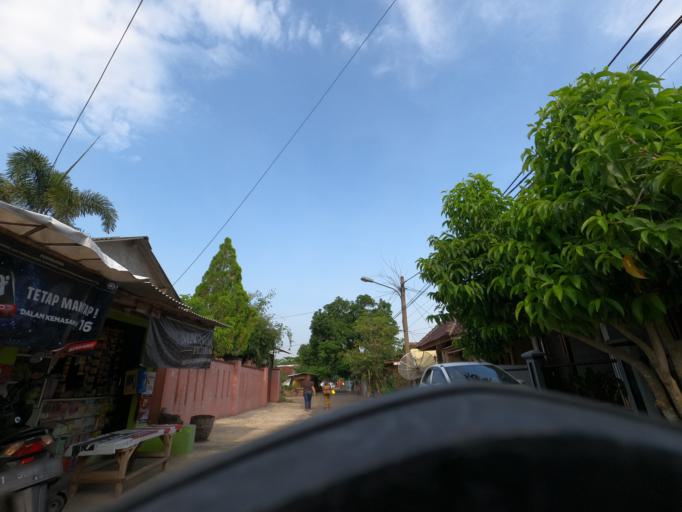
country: ID
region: West Java
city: Lembang
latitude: -6.5797
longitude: 107.7676
